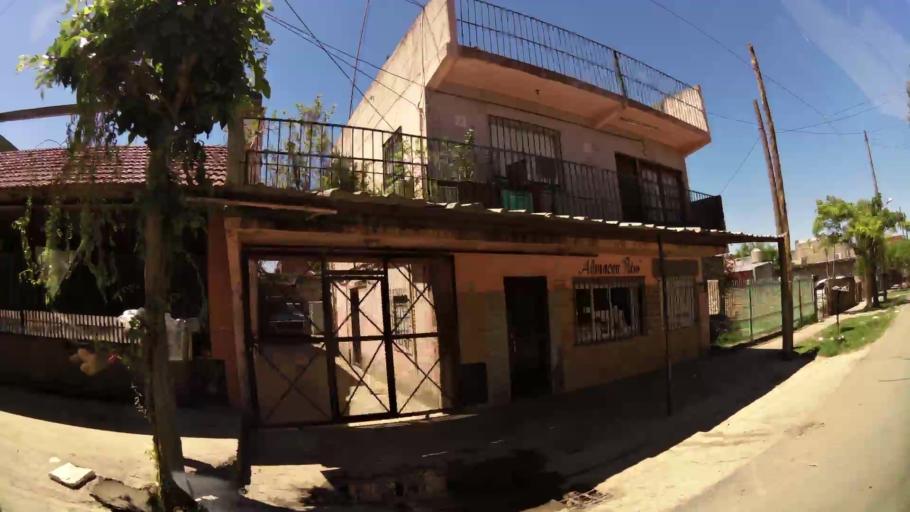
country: AR
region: Buenos Aires
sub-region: Partido de Quilmes
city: Quilmes
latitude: -34.7226
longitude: -58.3231
